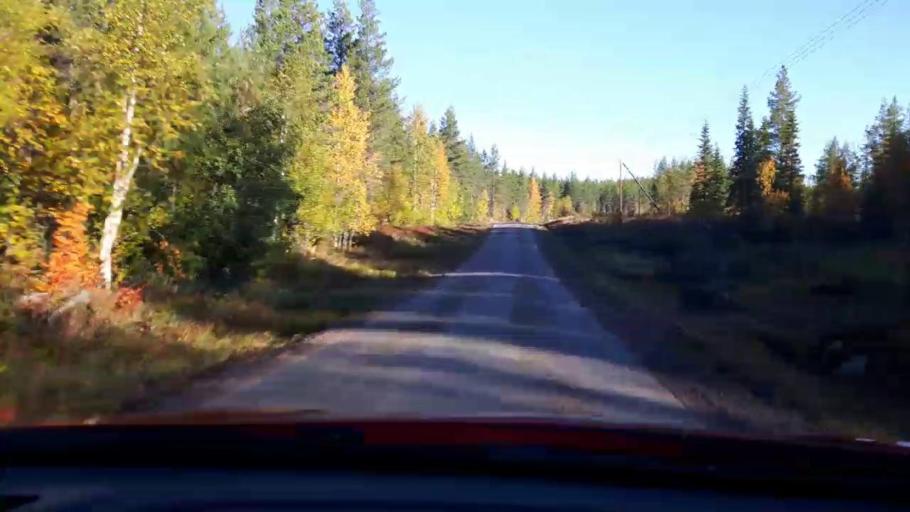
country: SE
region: Jaemtland
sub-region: Stroemsunds Kommun
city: Stroemsund
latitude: 64.3788
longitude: 15.1491
